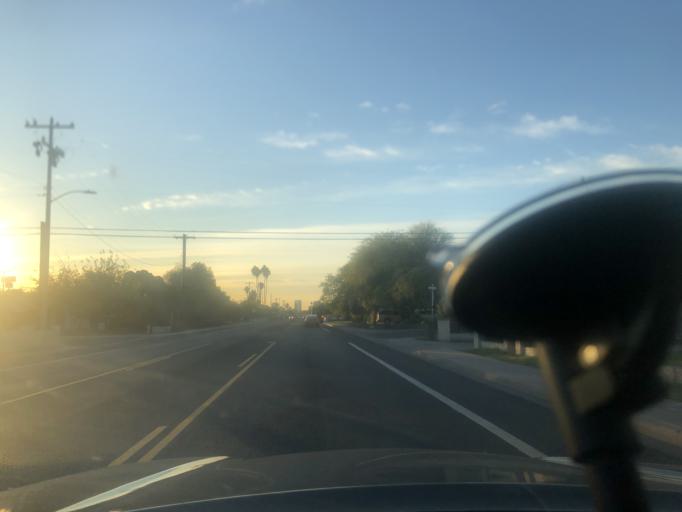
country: US
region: Arizona
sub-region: Maricopa County
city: Phoenix
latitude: 33.4876
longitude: -112.0341
